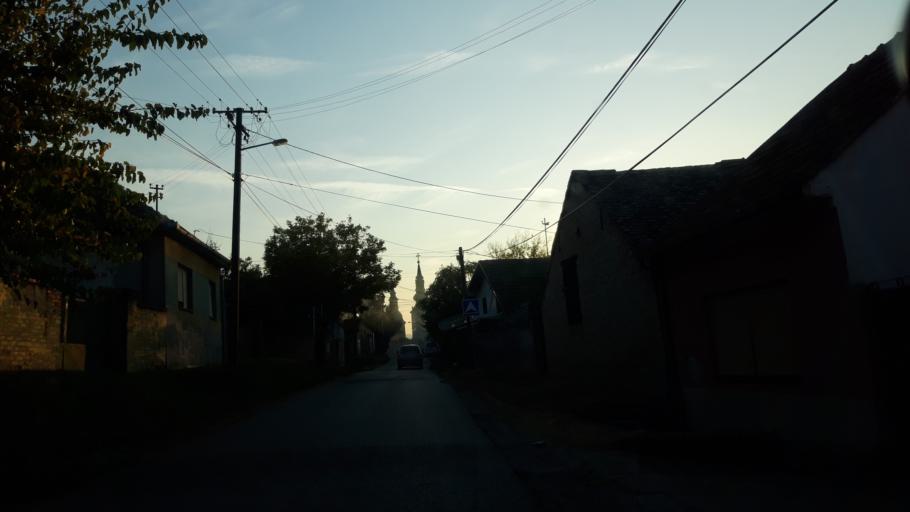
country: RS
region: Autonomna Pokrajina Vojvodina
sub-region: Juznobacki Okrug
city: Novi Sad
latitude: 45.2248
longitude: 19.8400
